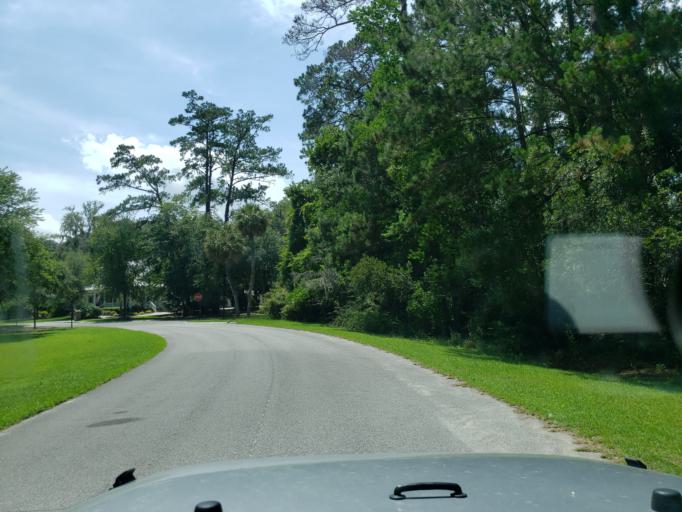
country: US
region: Georgia
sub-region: Chatham County
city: Whitemarsh Island
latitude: 32.0209
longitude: -81.0126
